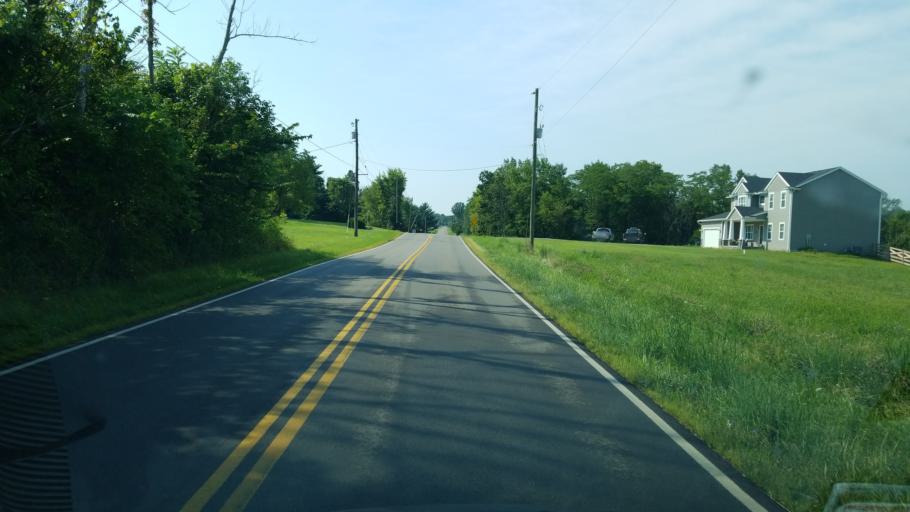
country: US
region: Ohio
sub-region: Richland County
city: Ontario
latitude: 40.8087
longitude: -82.6285
